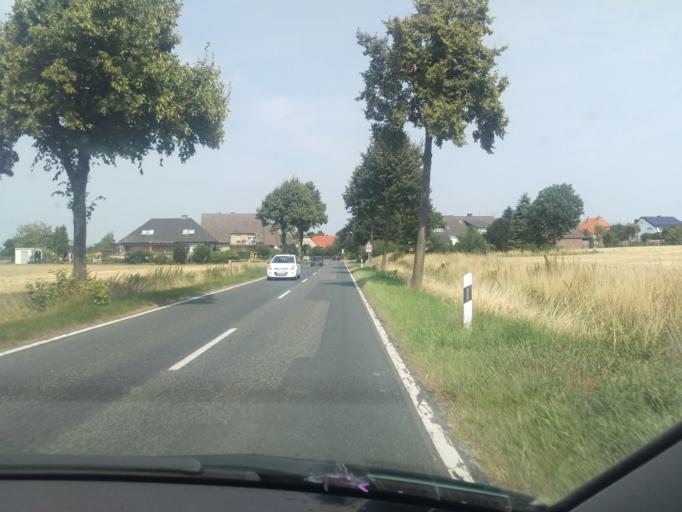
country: DE
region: Lower Saxony
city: Schellerten
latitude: 52.1655
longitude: 10.0894
